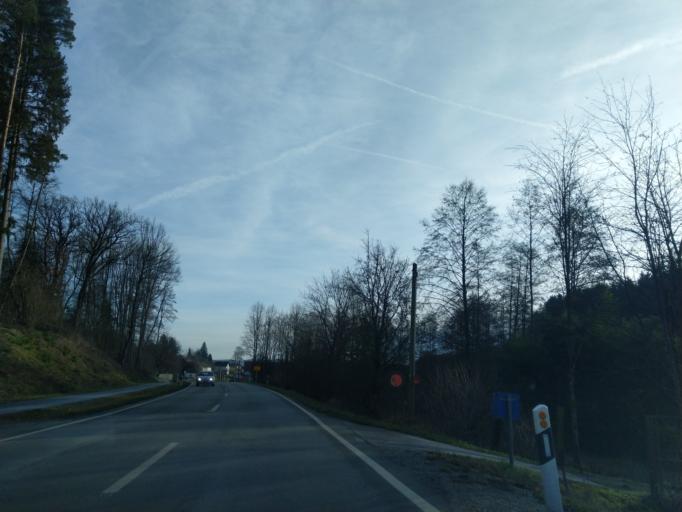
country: DE
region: Bavaria
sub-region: Lower Bavaria
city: Wallerfing
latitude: 48.6591
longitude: 12.8769
